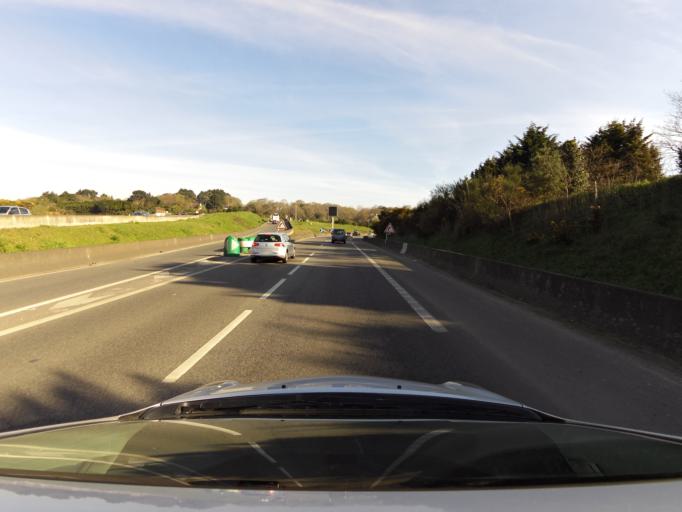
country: FR
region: Brittany
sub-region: Departement du Morbihan
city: Lorient
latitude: 47.7693
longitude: -3.3784
